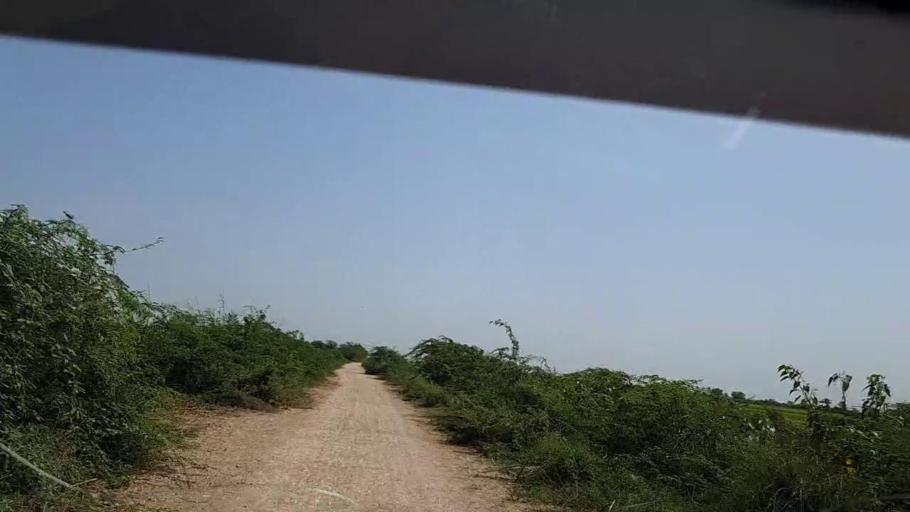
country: PK
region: Sindh
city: Rajo Khanani
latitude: 24.9362
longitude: 68.8766
